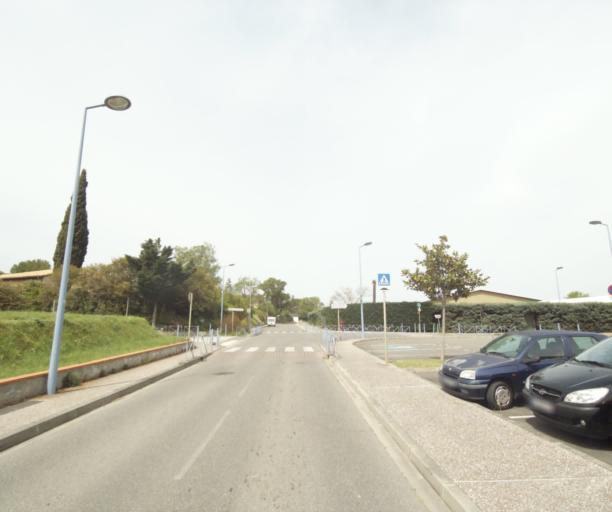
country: FR
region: Midi-Pyrenees
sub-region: Departement de la Haute-Garonne
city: Castanet-Tolosan
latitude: 43.5213
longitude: 1.4918
